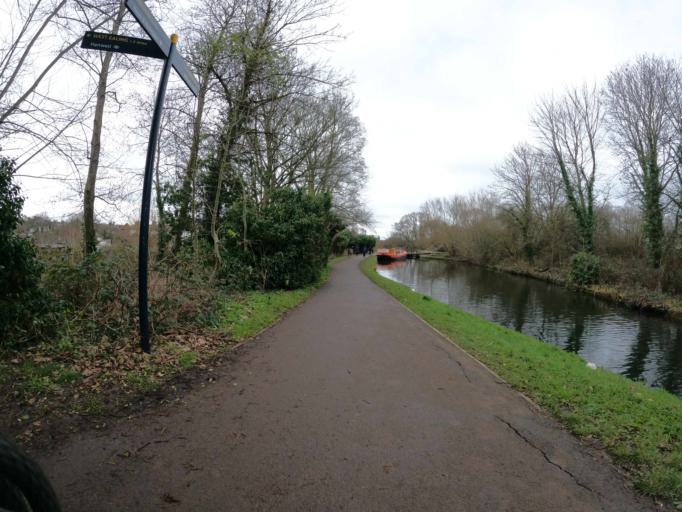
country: GB
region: England
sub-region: Greater London
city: Greenford
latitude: 51.5045
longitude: -0.3455
